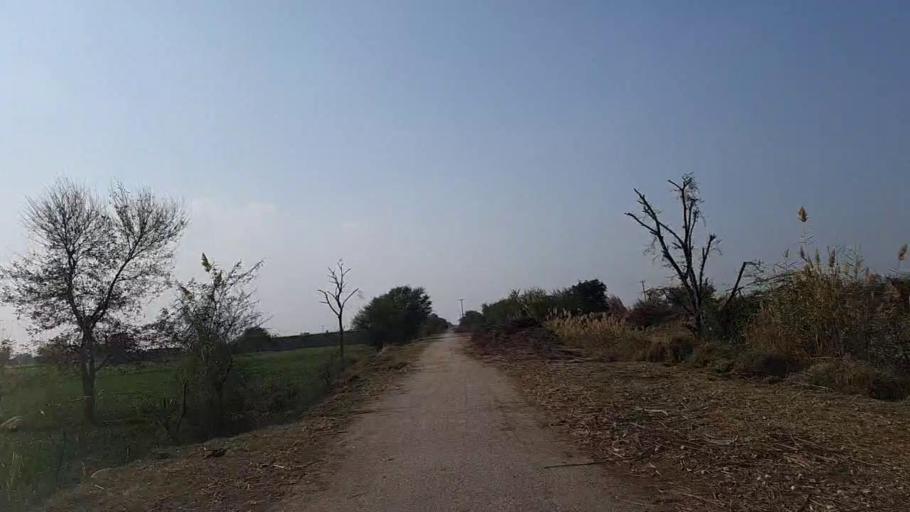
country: PK
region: Sindh
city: Jam Sahib
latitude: 26.2882
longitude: 68.5813
